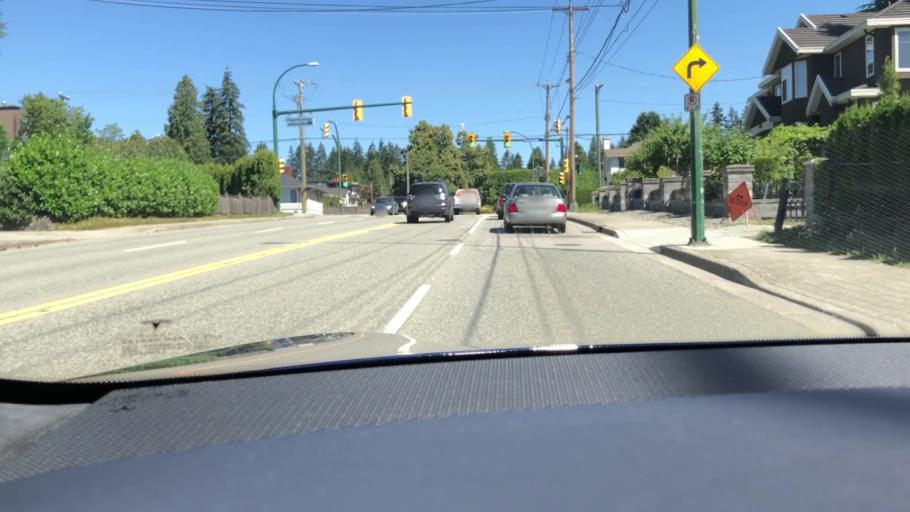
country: CA
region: British Columbia
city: Port Moody
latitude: 49.2448
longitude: -122.8728
